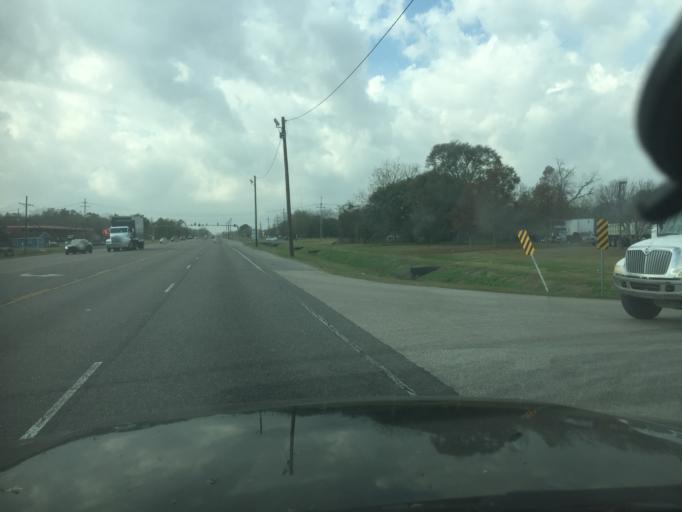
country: US
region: Louisiana
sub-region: Jefferson Parish
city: Avondale
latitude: 29.9104
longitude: -90.2091
